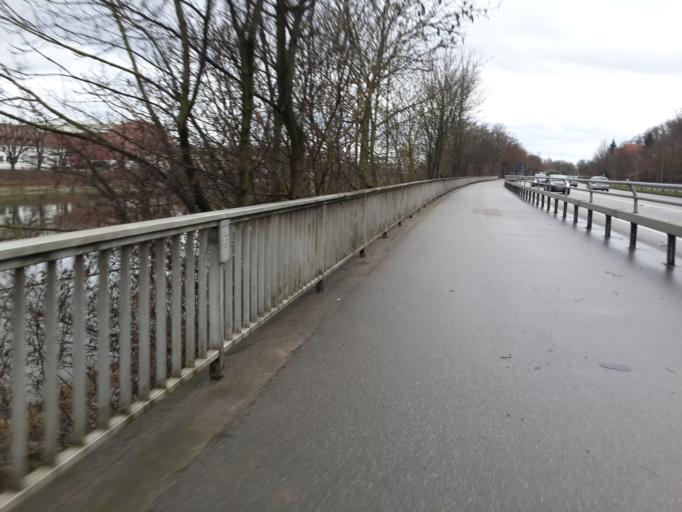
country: DE
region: Baden-Wuerttemberg
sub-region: Regierungsbezirk Stuttgart
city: Heilbronn
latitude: 49.1647
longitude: 9.2055
